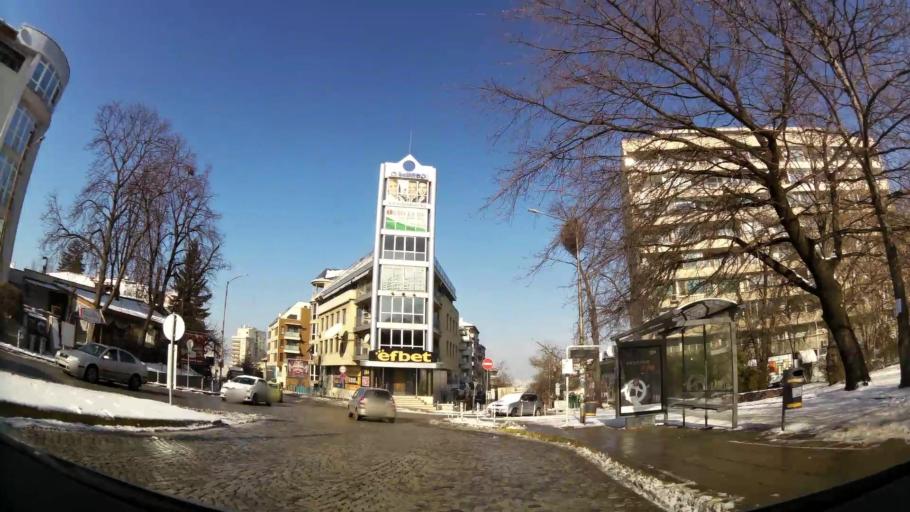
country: BG
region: Sofia-Capital
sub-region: Stolichna Obshtina
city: Sofia
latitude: 42.6766
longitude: 23.3336
